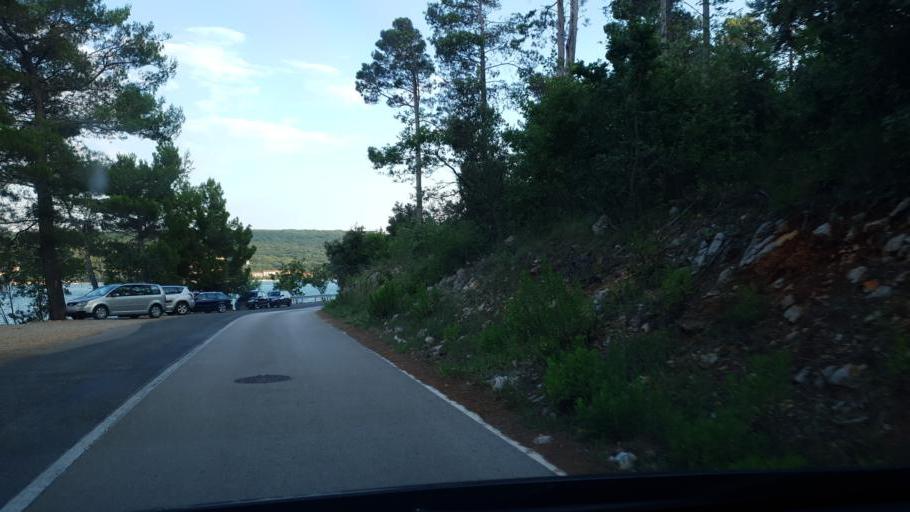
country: HR
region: Primorsko-Goranska
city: Njivice
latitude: 45.1604
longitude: 14.6022
